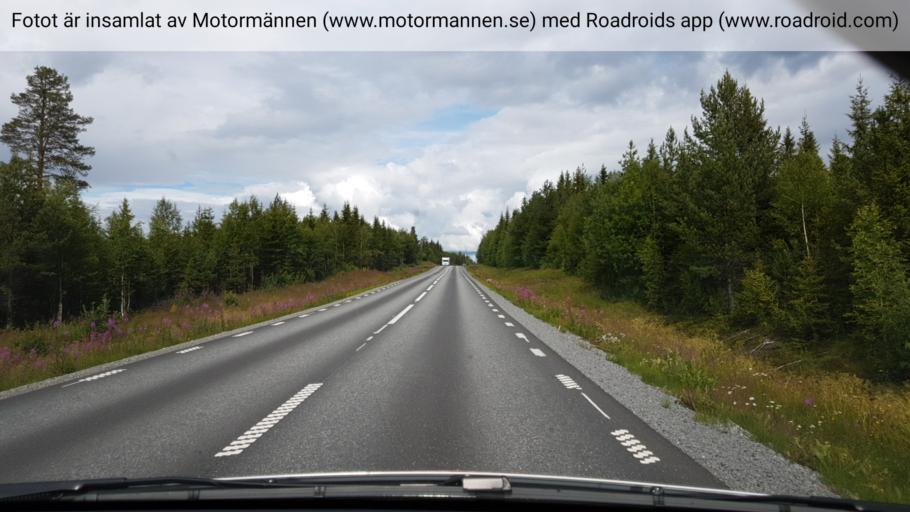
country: SE
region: Vaesterbotten
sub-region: Vilhelmina Kommun
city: Vilhelmina
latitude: 64.7094
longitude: 16.7072
